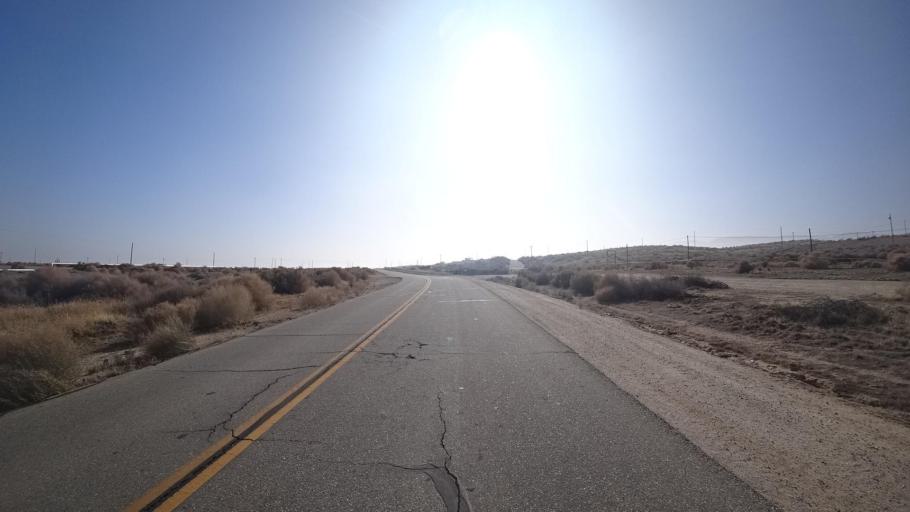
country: US
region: California
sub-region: Kern County
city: Taft Heights
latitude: 35.1677
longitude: -119.5330
